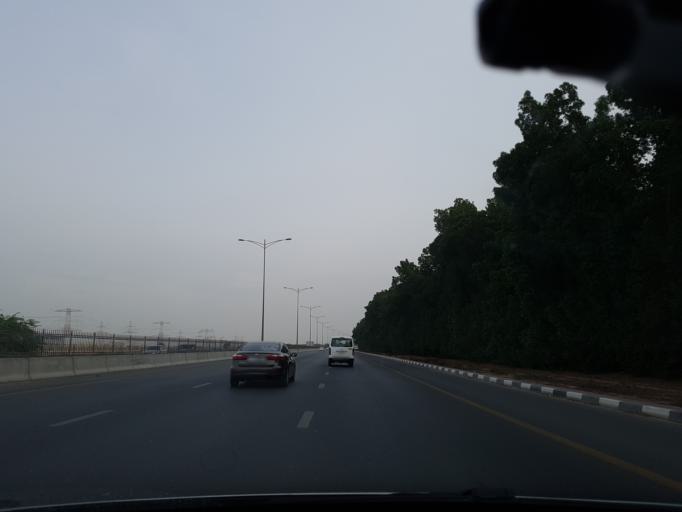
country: AE
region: Ajman
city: Ajman
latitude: 25.3648
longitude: 55.4710
